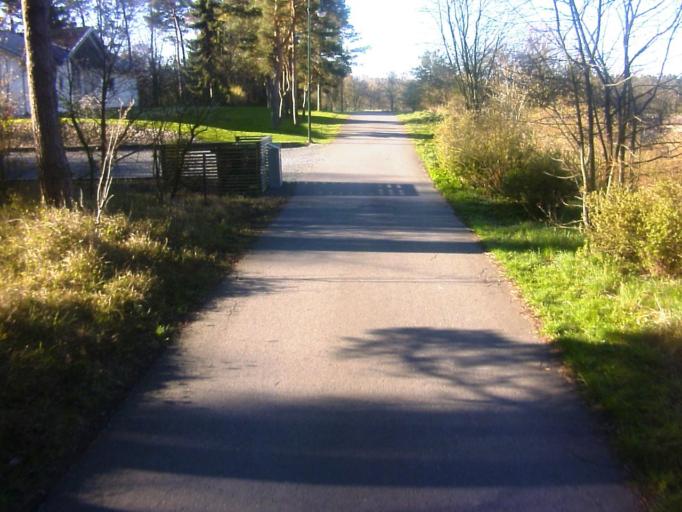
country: SE
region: Skane
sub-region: Kavlinge Kommun
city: Hofterup
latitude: 55.8141
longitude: 12.9687
